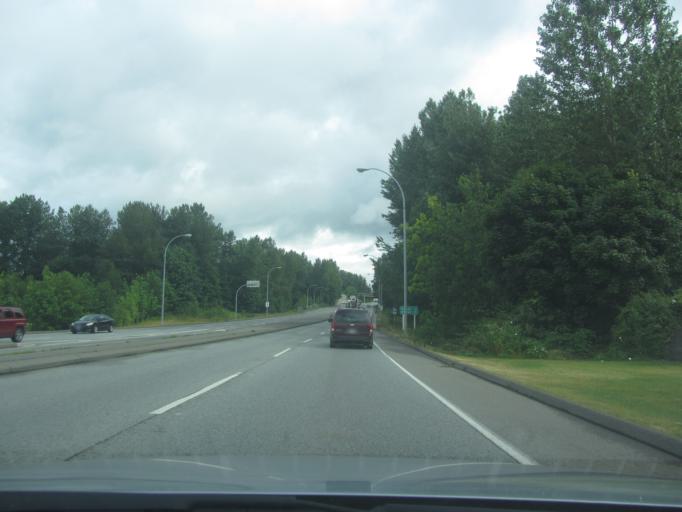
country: CA
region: British Columbia
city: Abbotsford
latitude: 49.0408
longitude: -122.2712
